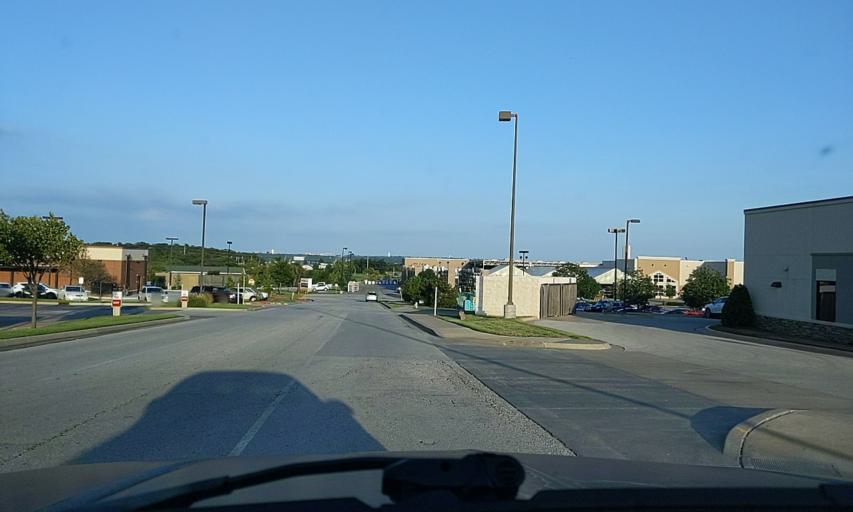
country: US
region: Oklahoma
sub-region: Tulsa County
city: Jenks
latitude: 36.0600
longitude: -96.0035
